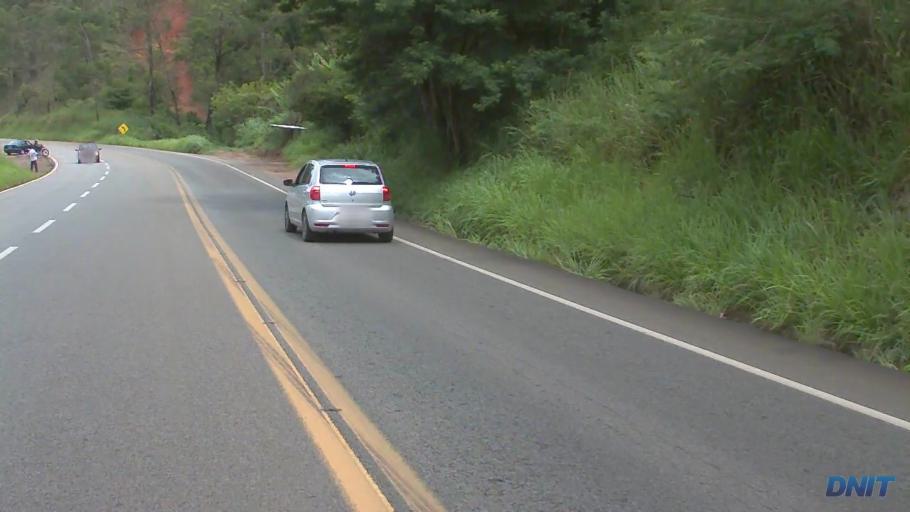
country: BR
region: Minas Gerais
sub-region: Nova Era
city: Nova Era
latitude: -19.8235
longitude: -43.0772
